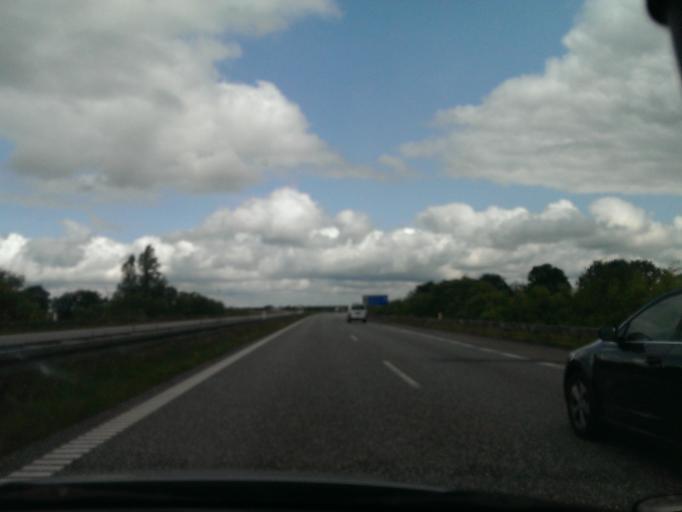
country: DK
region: North Denmark
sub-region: Mariagerfjord Kommune
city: Hobro
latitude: 56.6613
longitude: 9.7353
